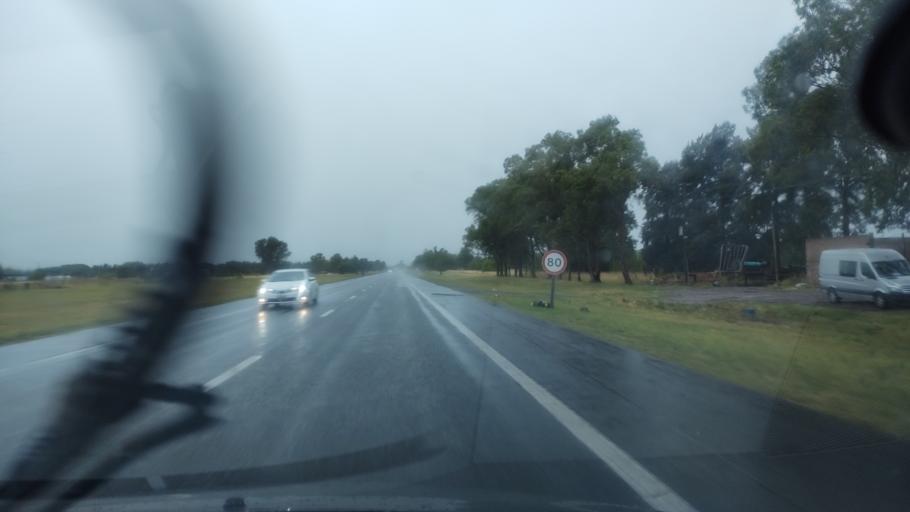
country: AR
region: Buenos Aires
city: Canuelas
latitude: -35.0591
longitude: -58.8005
